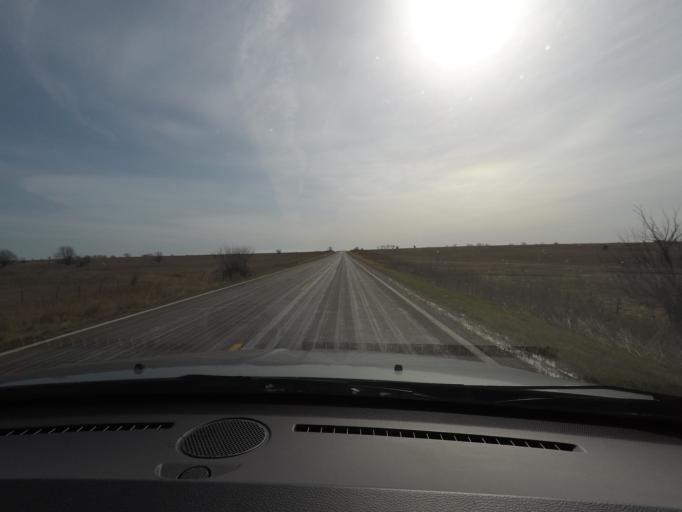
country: US
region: Kansas
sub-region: Lyon County
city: Emporia
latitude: 38.6588
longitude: -96.1959
